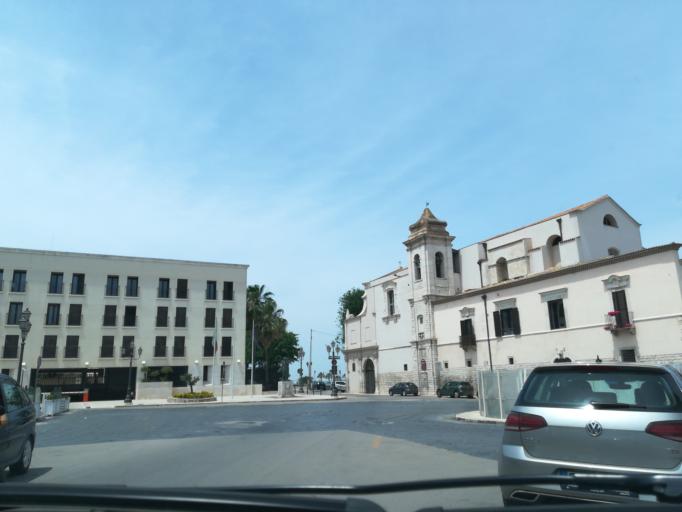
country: IT
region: Apulia
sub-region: Provincia di Barletta - Andria - Trani
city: Barletta
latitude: 41.3220
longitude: 16.2847
